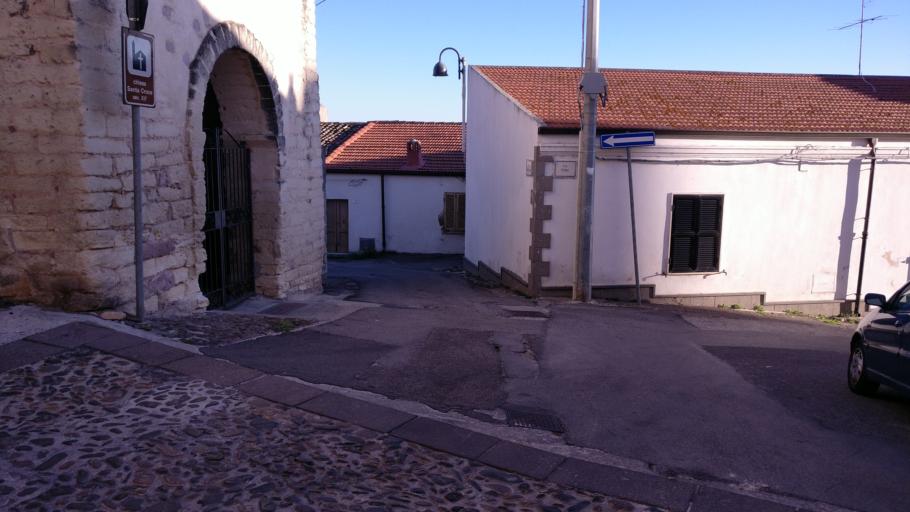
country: IT
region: Sardinia
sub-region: Provincia di Sassari
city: Uri
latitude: 40.6344
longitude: 8.4914
